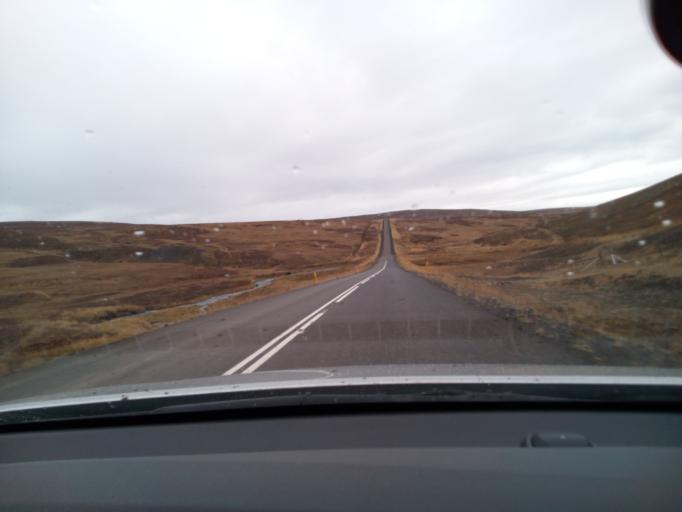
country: IS
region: Northeast
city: Laugar
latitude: 65.7937
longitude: -17.2368
